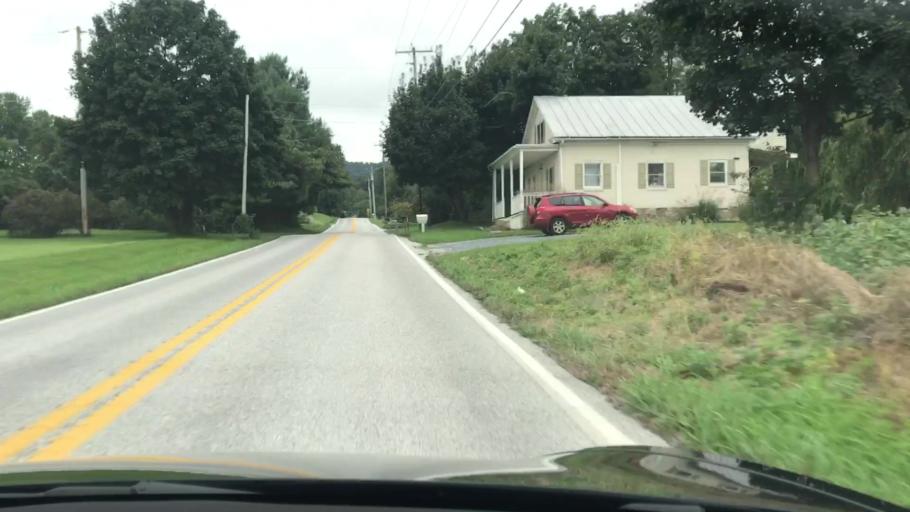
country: US
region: Pennsylvania
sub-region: York County
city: Dillsburg
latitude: 40.1230
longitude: -76.9592
